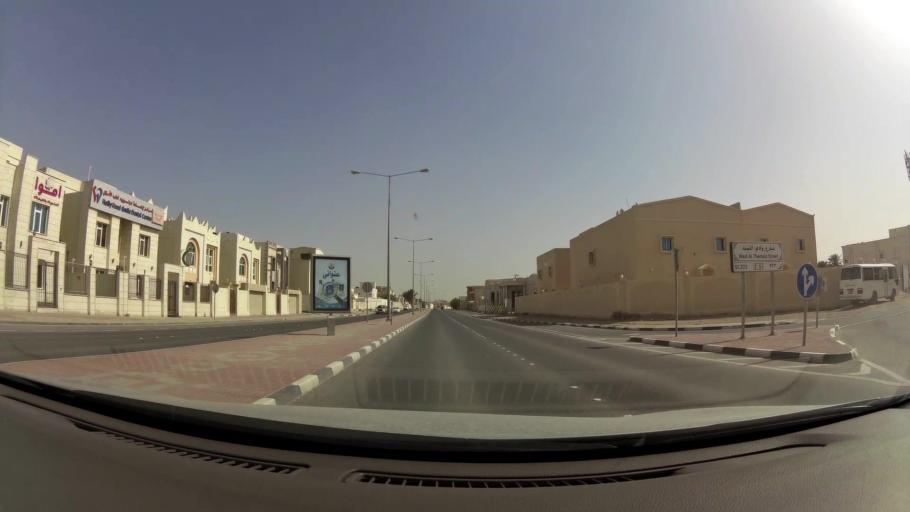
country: QA
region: Baladiyat Umm Salal
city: Umm Salal Muhammad
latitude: 25.3612
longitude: 51.4372
